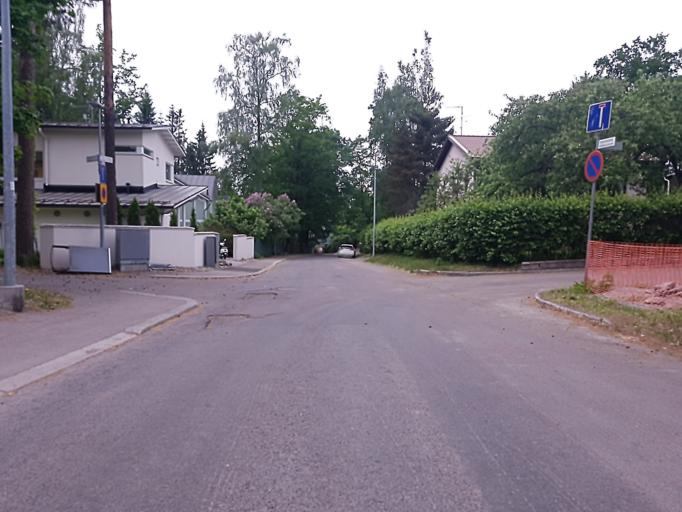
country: FI
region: Uusimaa
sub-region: Helsinki
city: Helsinki
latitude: 60.2256
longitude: 24.9711
